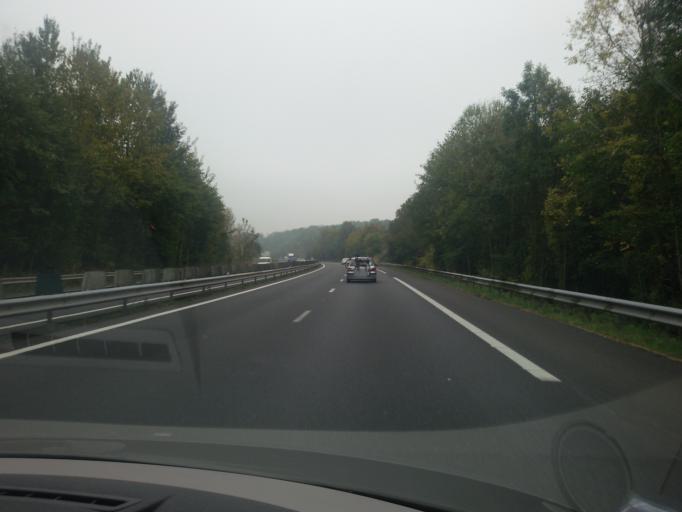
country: FR
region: Lower Normandy
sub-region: Departement du Calvados
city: Dozule
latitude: 49.2469
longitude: 0.0342
